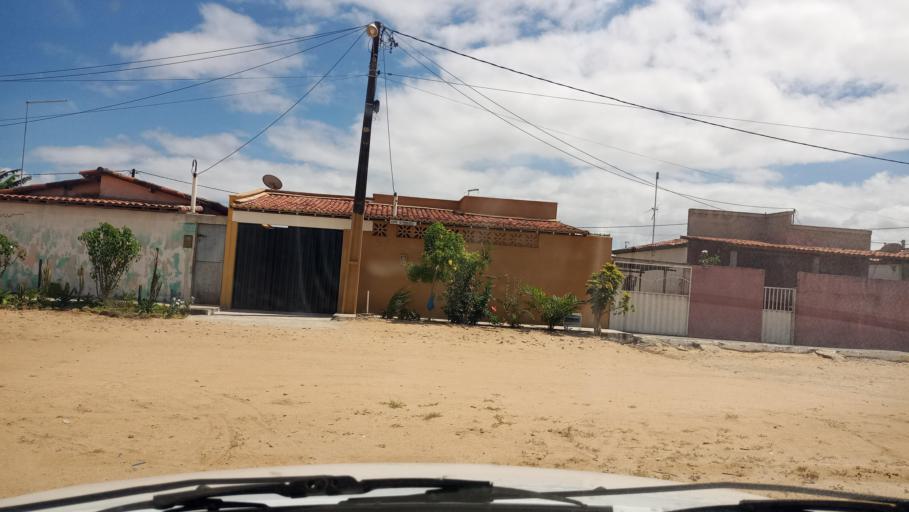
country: BR
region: Rio Grande do Norte
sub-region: Brejinho
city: Brejinho
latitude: -6.2046
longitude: -35.3457
